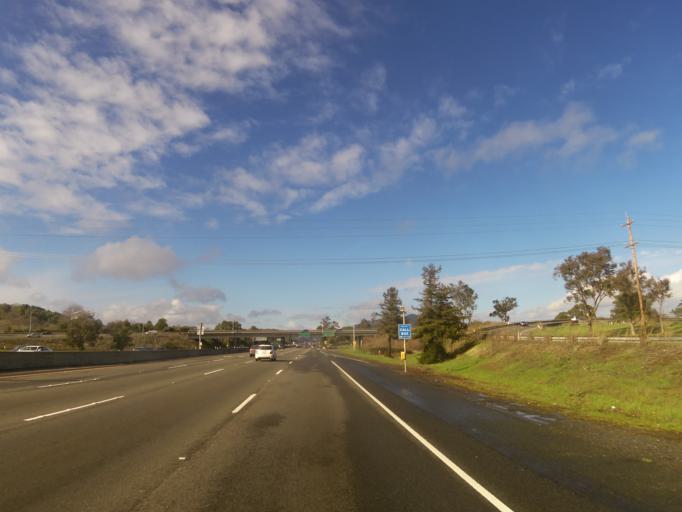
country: US
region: California
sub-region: Marin County
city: Novato
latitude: 38.0782
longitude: -122.5441
